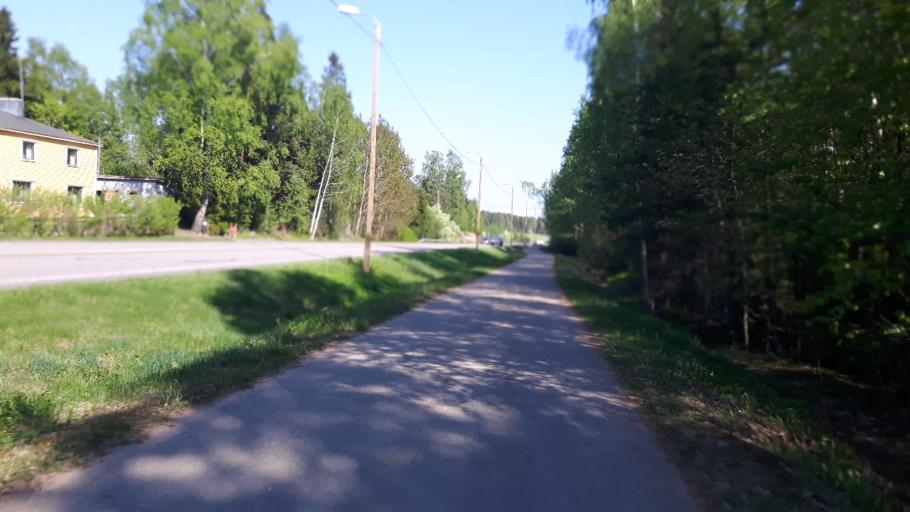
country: FI
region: Kymenlaakso
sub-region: Kotka-Hamina
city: Broby
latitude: 60.4970
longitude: 26.7871
